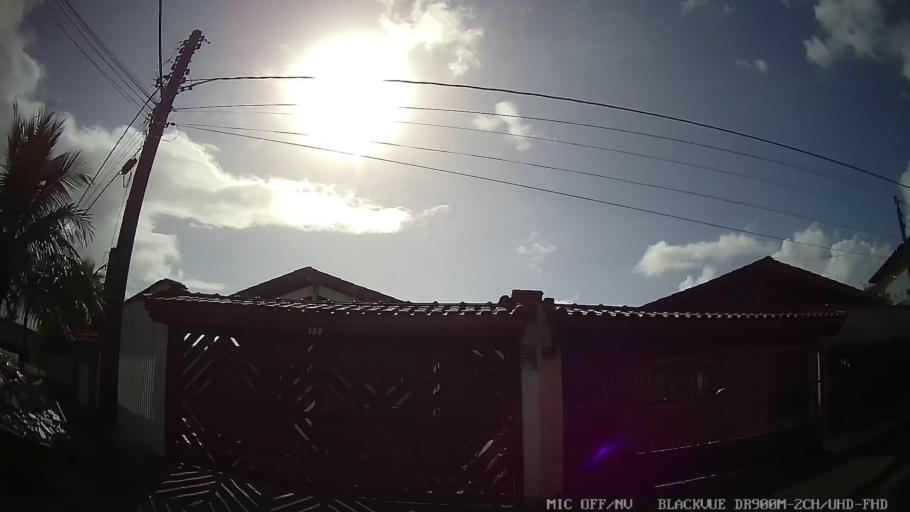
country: BR
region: Sao Paulo
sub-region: Itanhaem
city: Itanhaem
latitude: -24.2088
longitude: -46.8355
